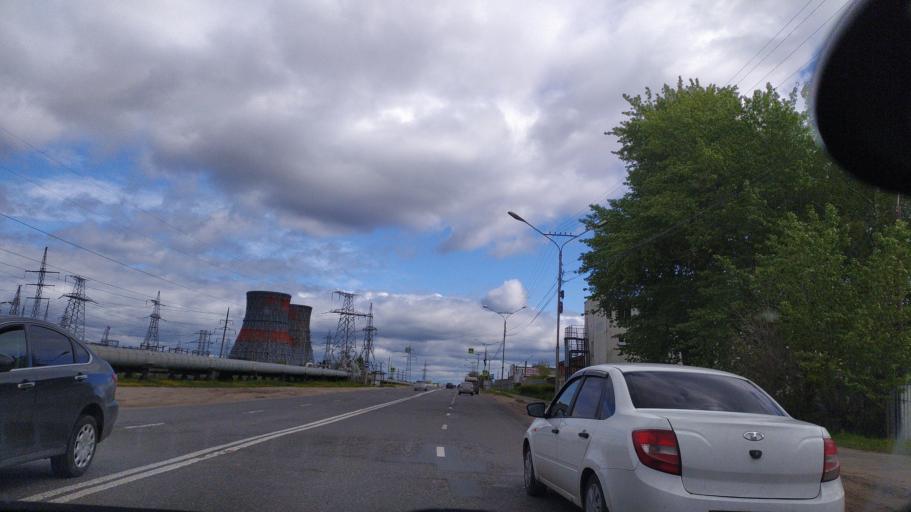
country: RU
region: Chuvashia
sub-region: Cheboksarskiy Rayon
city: Cheboksary
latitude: 56.1199
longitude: 47.3022
